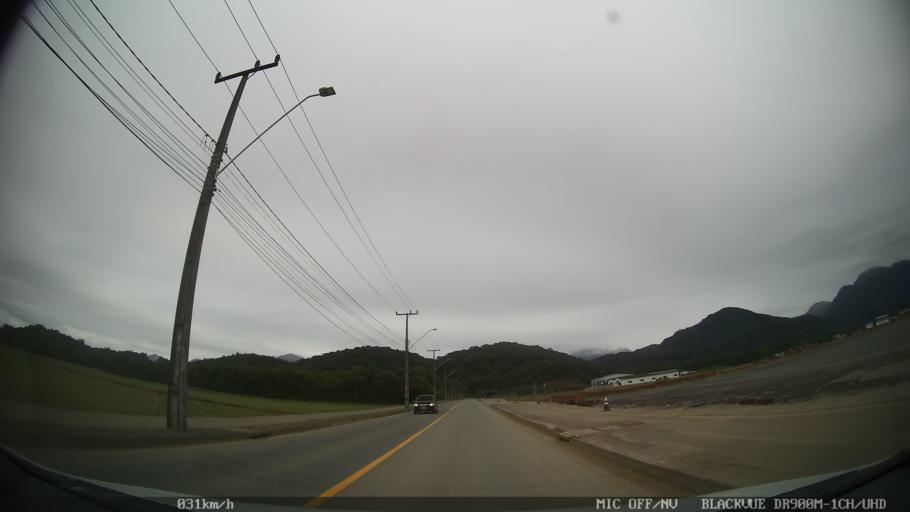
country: BR
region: Santa Catarina
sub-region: Joinville
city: Joinville
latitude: -26.2781
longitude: -48.9197
